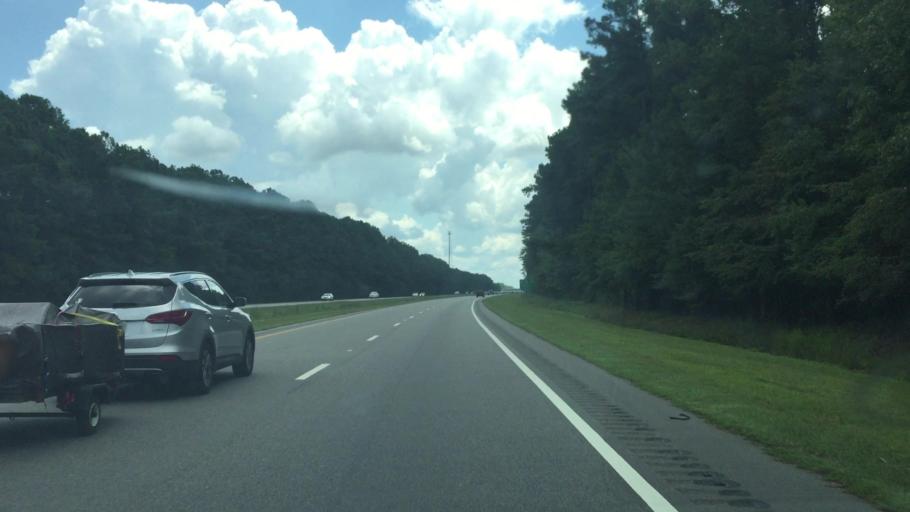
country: US
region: North Carolina
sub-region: Columbus County
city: Chadbourn
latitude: 34.3760
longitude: -78.8477
